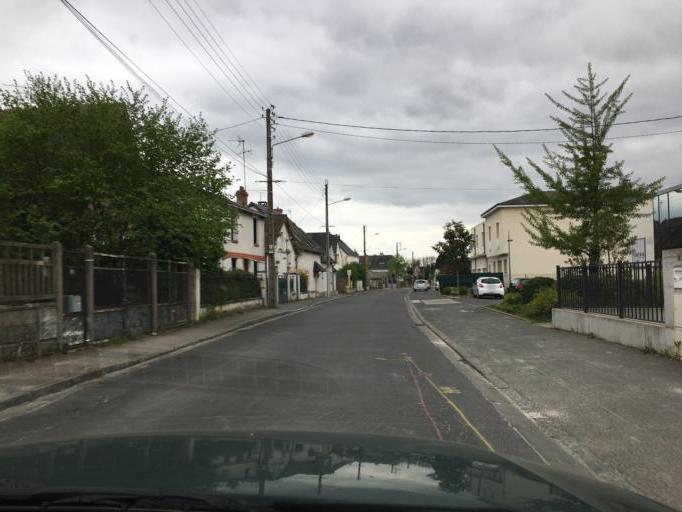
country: FR
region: Centre
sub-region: Departement du Loiret
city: Saint-Jean-de-la-Ruelle
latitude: 47.9120
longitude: 1.8731
